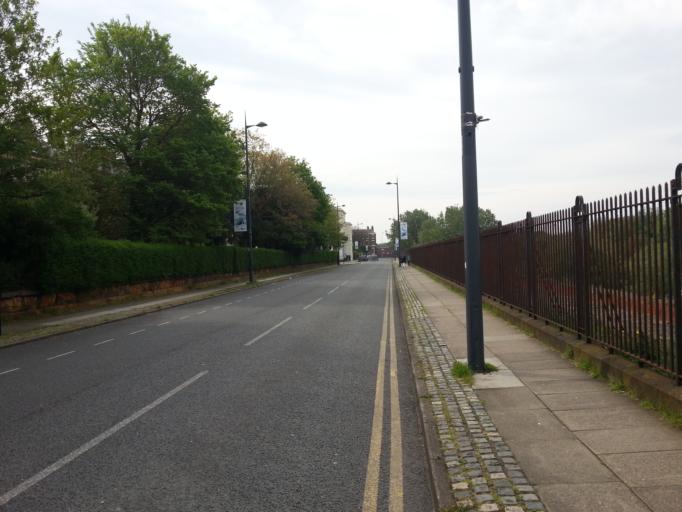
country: GB
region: England
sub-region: Liverpool
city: Liverpool
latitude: 53.3978
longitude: -2.9713
